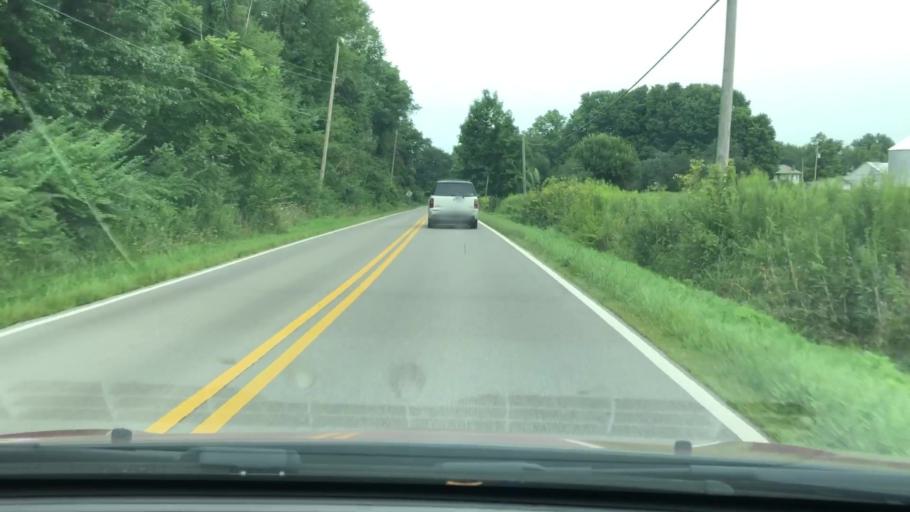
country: US
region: Ohio
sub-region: Delaware County
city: Sunbury
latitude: 40.1863
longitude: -82.8527
